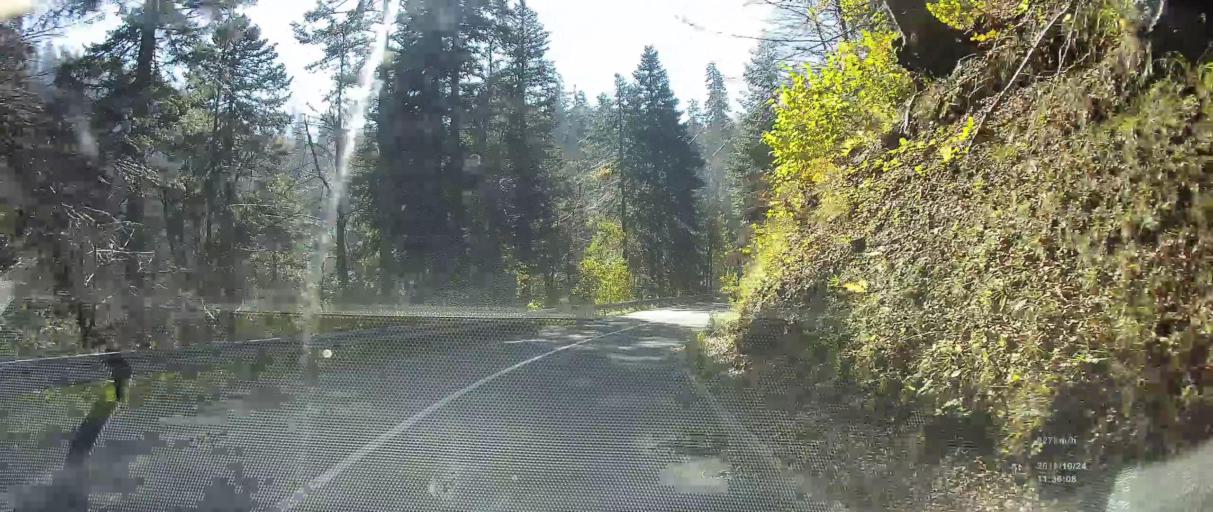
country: HR
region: Primorsko-Goranska
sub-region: Grad Delnice
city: Delnice
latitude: 45.3968
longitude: 14.7007
